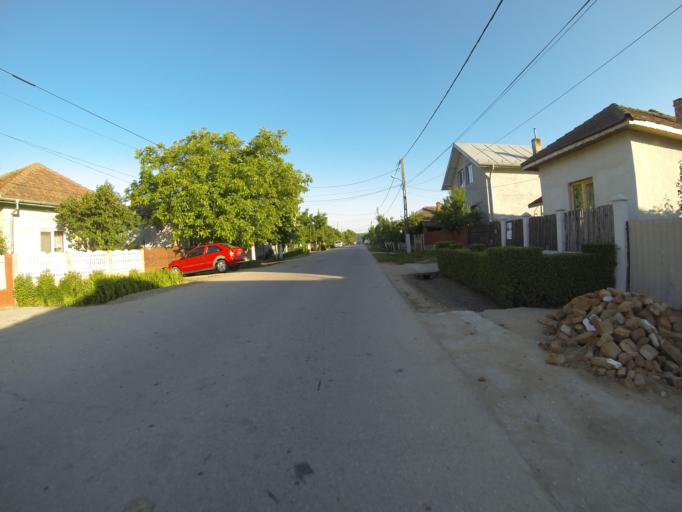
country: RO
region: Dolj
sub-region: Comuna Tuglui
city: Tuglui
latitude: 44.1897
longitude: 23.8116
